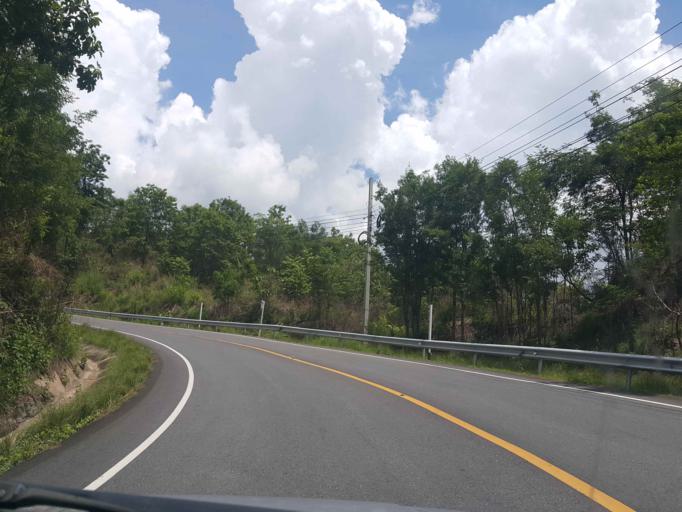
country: TH
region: Phayao
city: Chiang Muan
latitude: 18.8420
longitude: 100.3514
